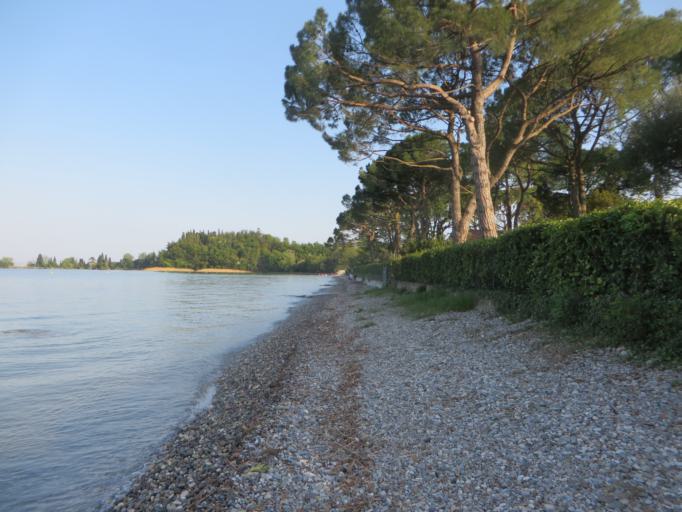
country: IT
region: Lombardy
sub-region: Provincia di Brescia
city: San Felice del Benaco
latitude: 45.5924
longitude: 10.5684
